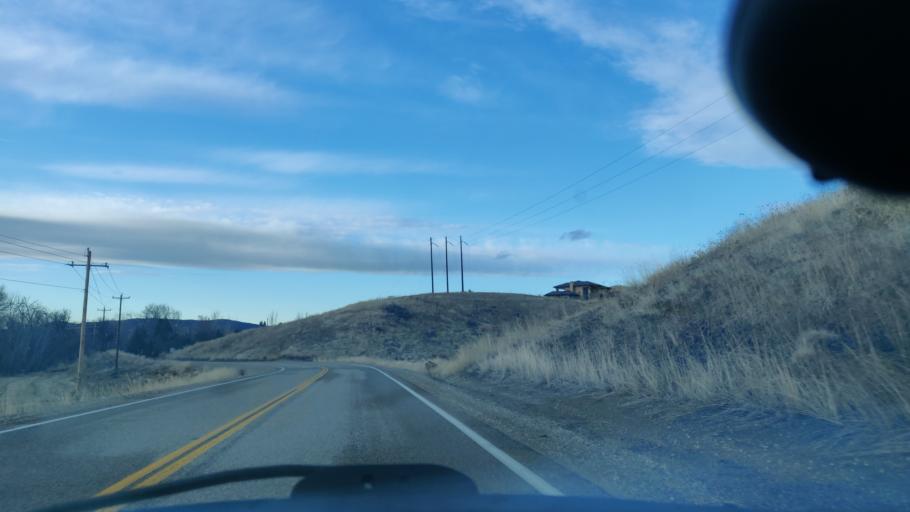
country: US
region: Idaho
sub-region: Ada County
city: Garden City
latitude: 43.7267
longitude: -116.2504
